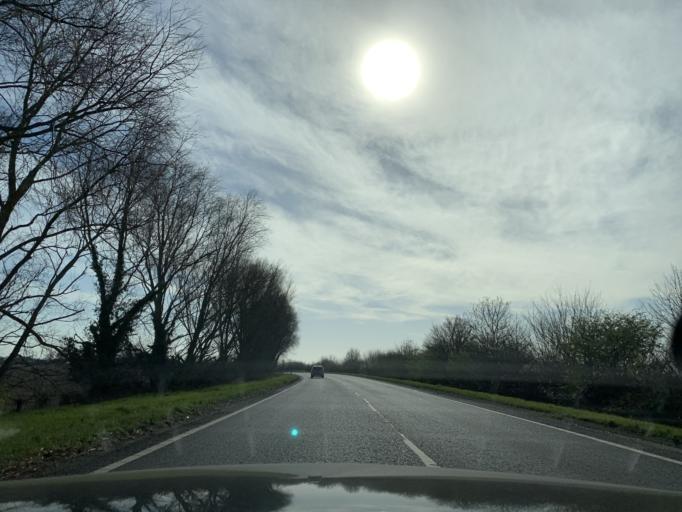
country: GB
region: England
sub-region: Kent
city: Romney Marsh
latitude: 51.0143
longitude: 0.8629
